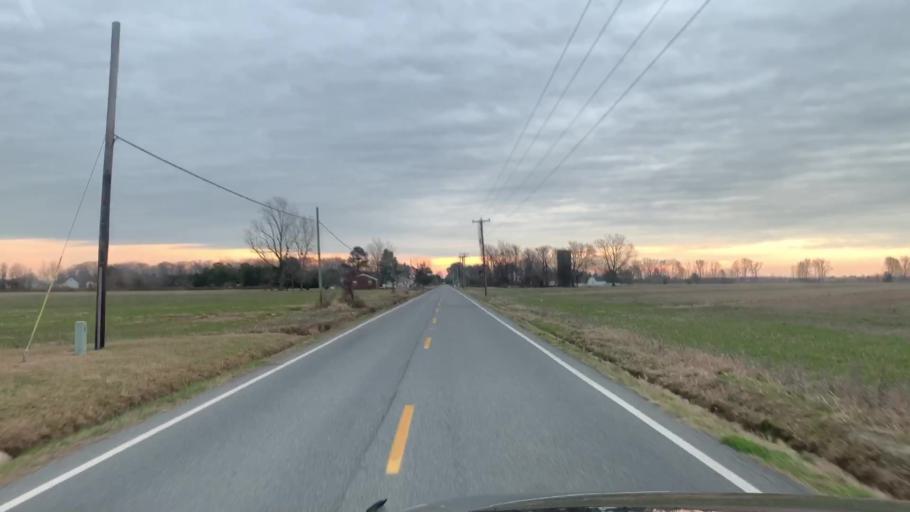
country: US
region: North Carolina
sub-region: Currituck County
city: Moyock
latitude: 36.6277
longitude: -76.1679
